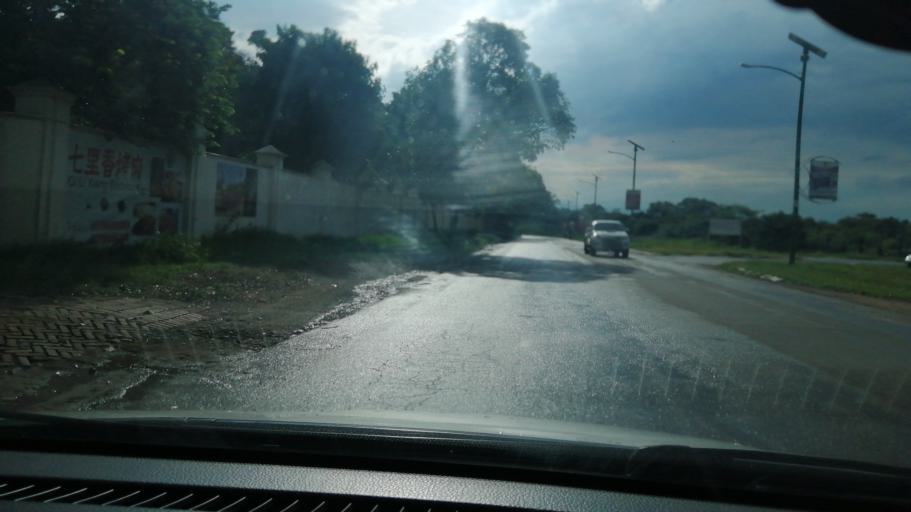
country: ZW
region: Harare
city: Harare
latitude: -17.7906
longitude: 31.0487
